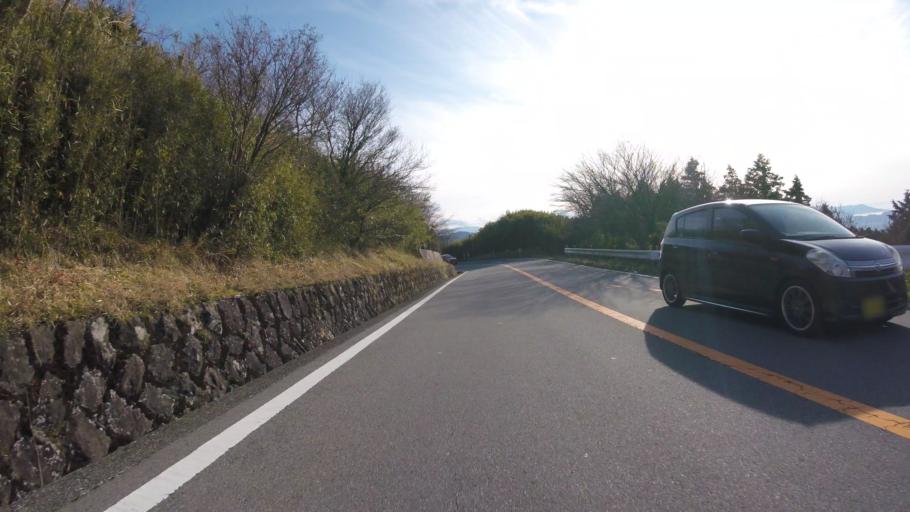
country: JP
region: Kanagawa
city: Yugawara
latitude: 35.1384
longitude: 139.0341
